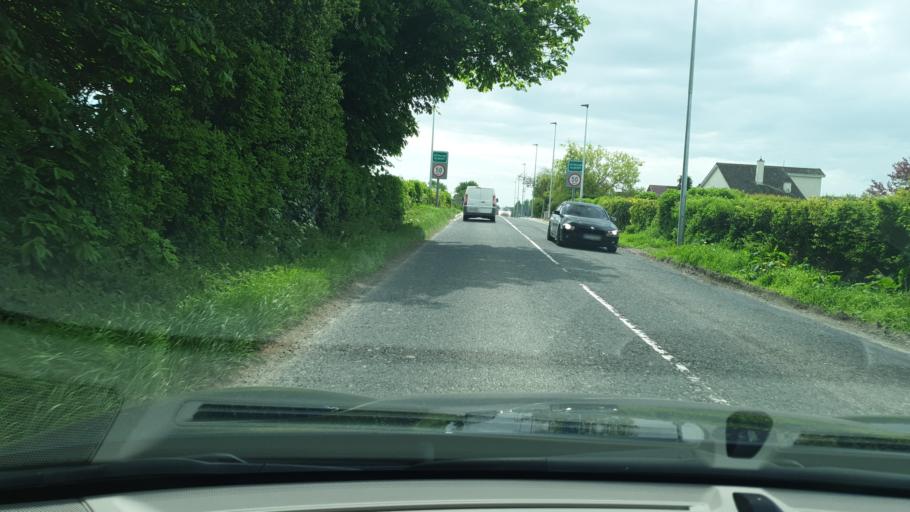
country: IE
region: Leinster
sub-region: An Mhi
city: Navan
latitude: 53.7085
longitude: -6.6877
